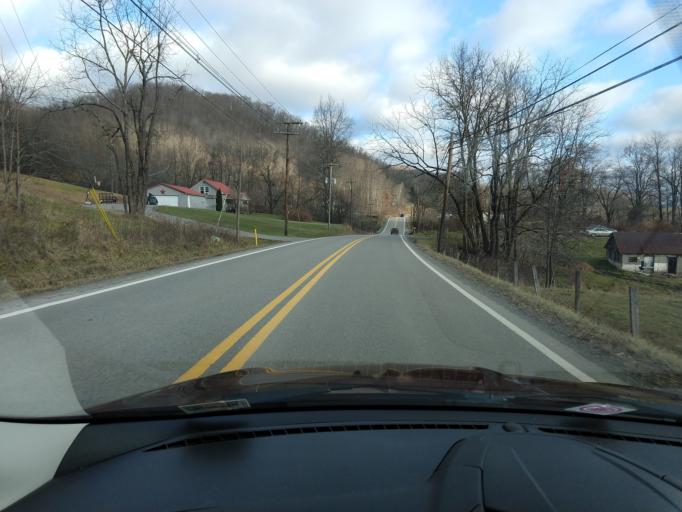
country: US
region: West Virginia
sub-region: Randolph County
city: Elkins
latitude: 38.7417
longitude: -79.9650
